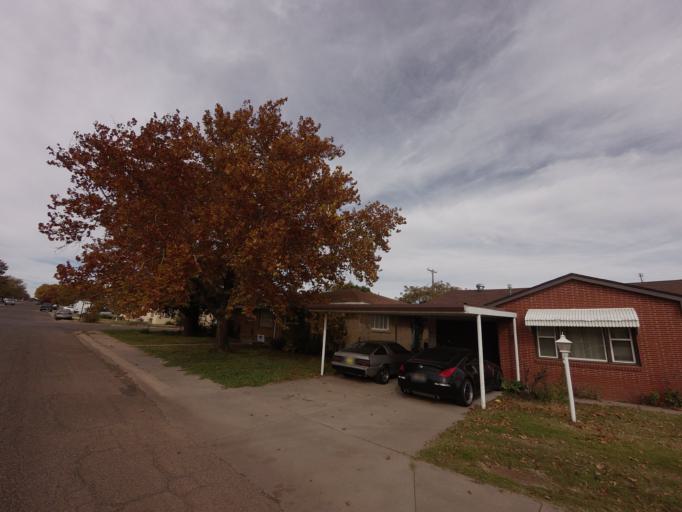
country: US
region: New Mexico
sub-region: Curry County
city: Clovis
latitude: 34.4262
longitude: -103.2091
